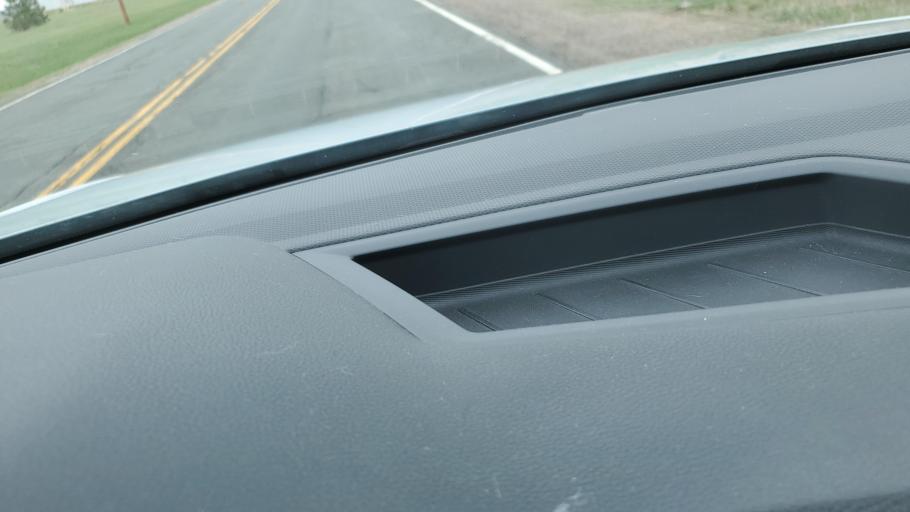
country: US
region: Colorado
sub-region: Weld County
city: Lochbuie
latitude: 39.9723
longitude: -104.7361
